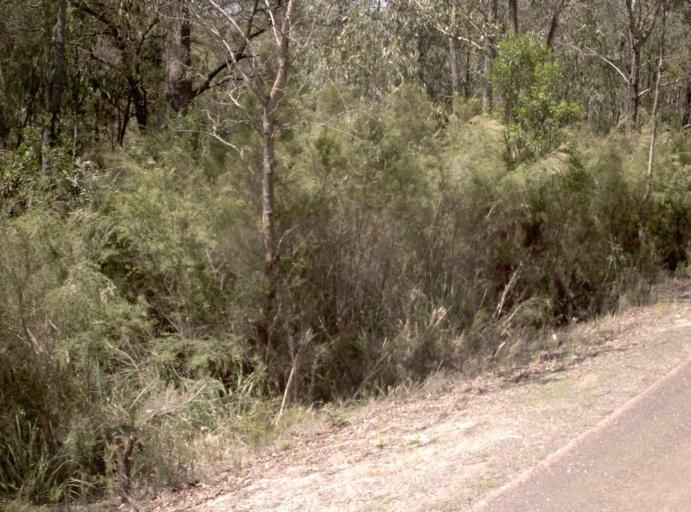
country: AU
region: New South Wales
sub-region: Bombala
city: Bombala
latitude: -37.5659
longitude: 149.0873
